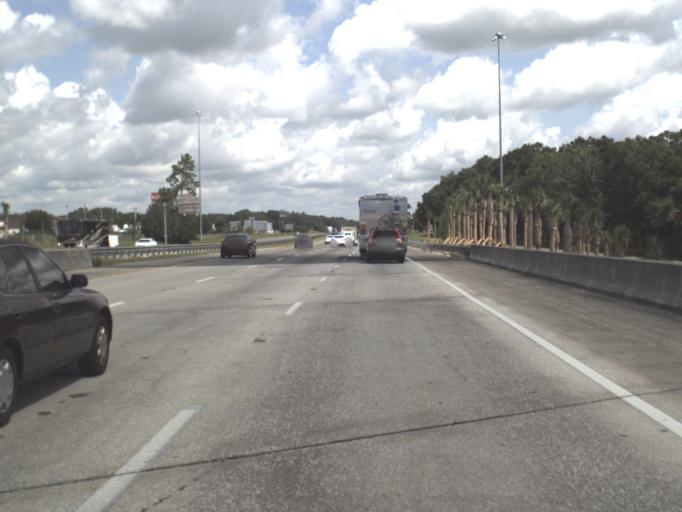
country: US
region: Florida
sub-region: Columbia County
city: Lake City
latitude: 30.1178
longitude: -82.6557
